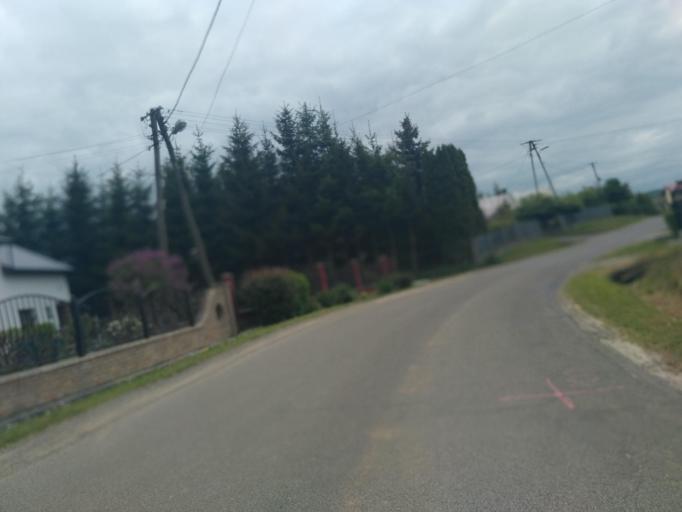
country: PL
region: Subcarpathian Voivodeship
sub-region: Powiat krosnienski
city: Jedlicze
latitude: 49.7005
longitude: 21.6403
